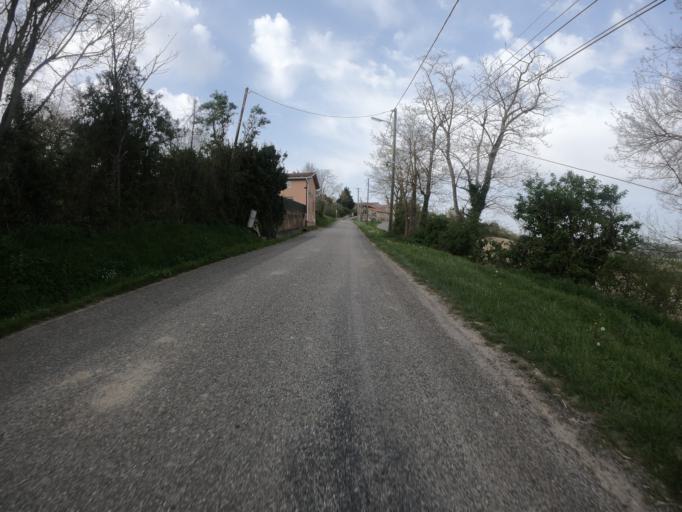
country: FR
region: Midi-Pyrenees
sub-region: Departement de l'Ariege
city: La Tour-du-Crieu
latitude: 43.1405
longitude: 1.7125
